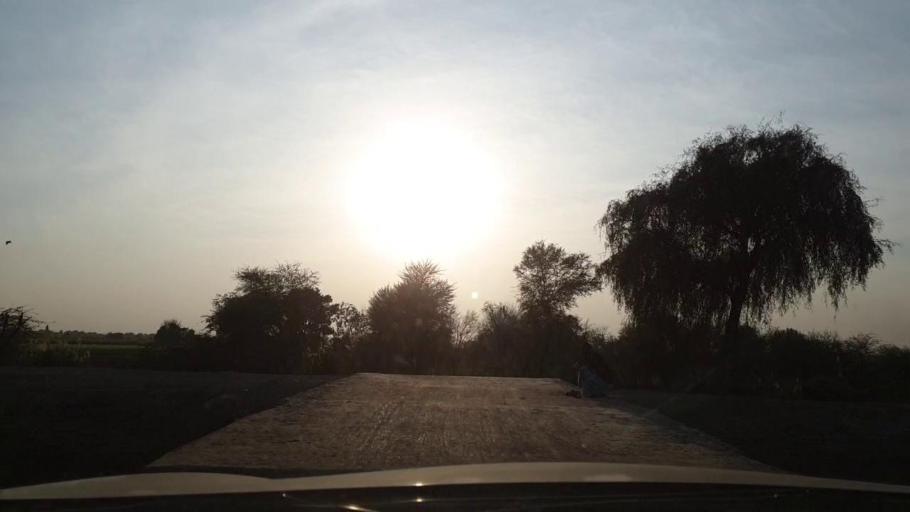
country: PK
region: Sindh
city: Tando Adam
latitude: 25.7083
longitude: 68.7350
